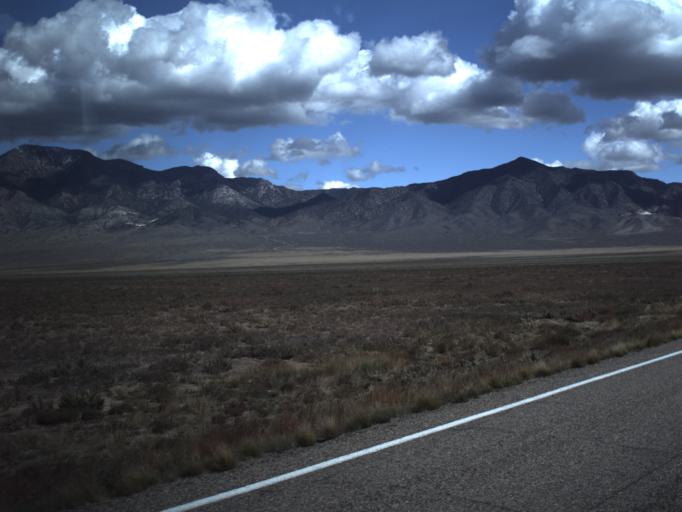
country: US
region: Utah
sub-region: Beaver County
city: Milford
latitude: 38.4657
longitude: -113.3923
